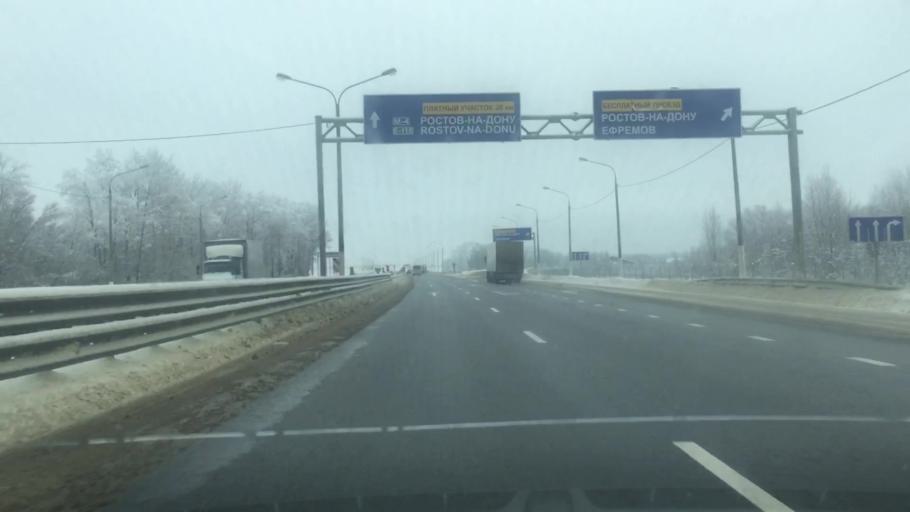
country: RU
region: Tula
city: Kazachka
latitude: 53.2951
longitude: 38.1780
